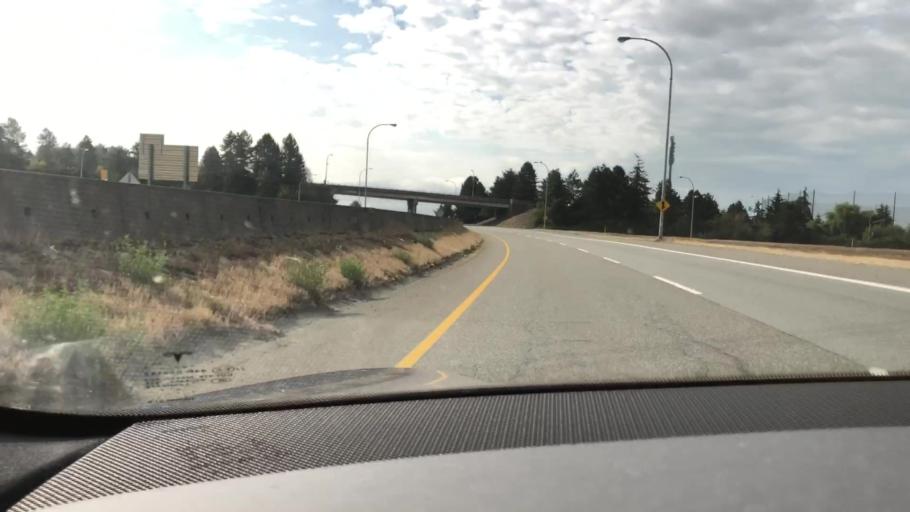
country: CA
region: British Columbia
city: Delta
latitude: 49.1214
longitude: -122.9277
